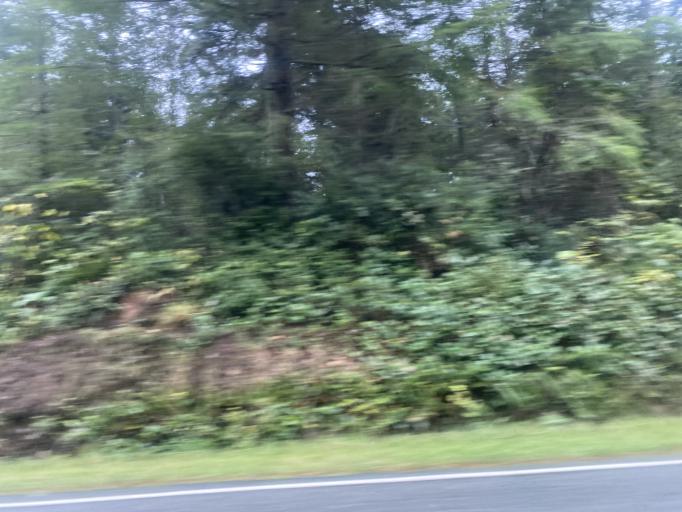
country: US
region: Washington
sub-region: Island County
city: Freeland
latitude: 48.0660
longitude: -122.4976
